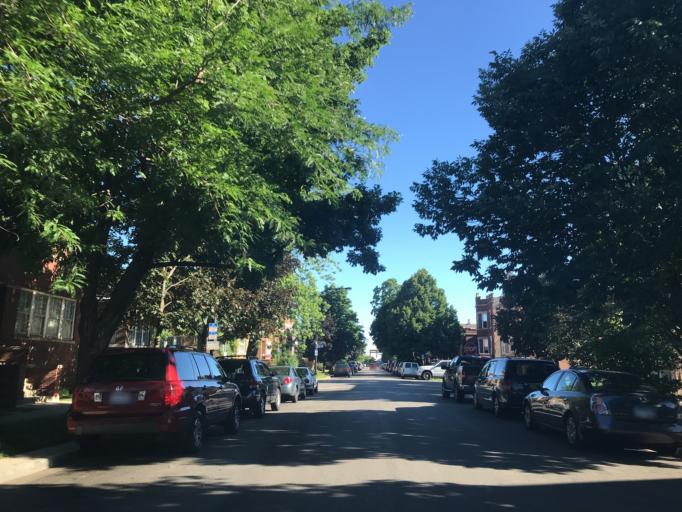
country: US
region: Illinois
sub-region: Cook County
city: Cicero
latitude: 41.8461
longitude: -87.7663
